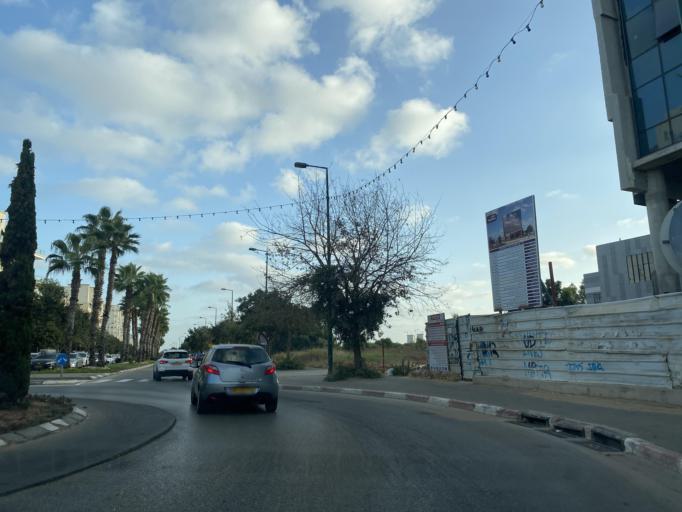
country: IL
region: Central District
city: Netanya
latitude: 32.3104
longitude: 34.8698
